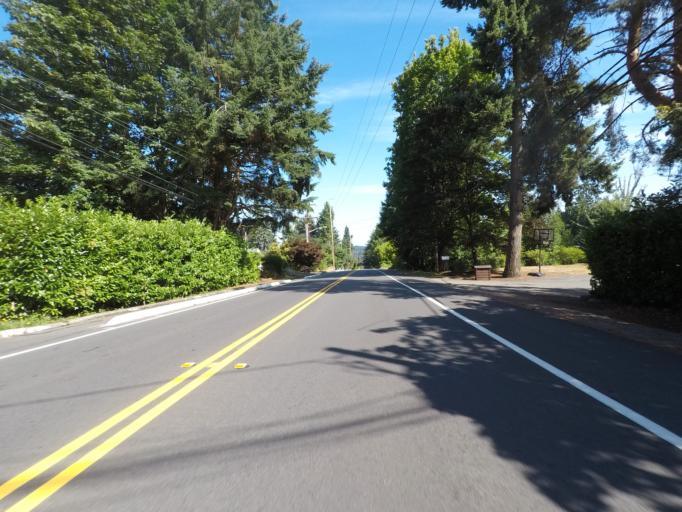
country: US
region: Washington
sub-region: King County
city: Inglewood-Finn Hill
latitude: 47.7415
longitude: -122.2289
